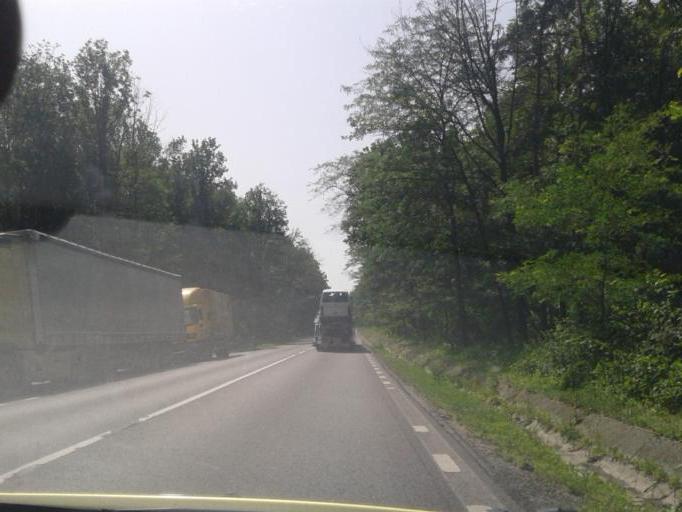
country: RO
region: Arges
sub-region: Comuna Cotmeana
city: Cotmeana
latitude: 44.9808
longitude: 24.6565
